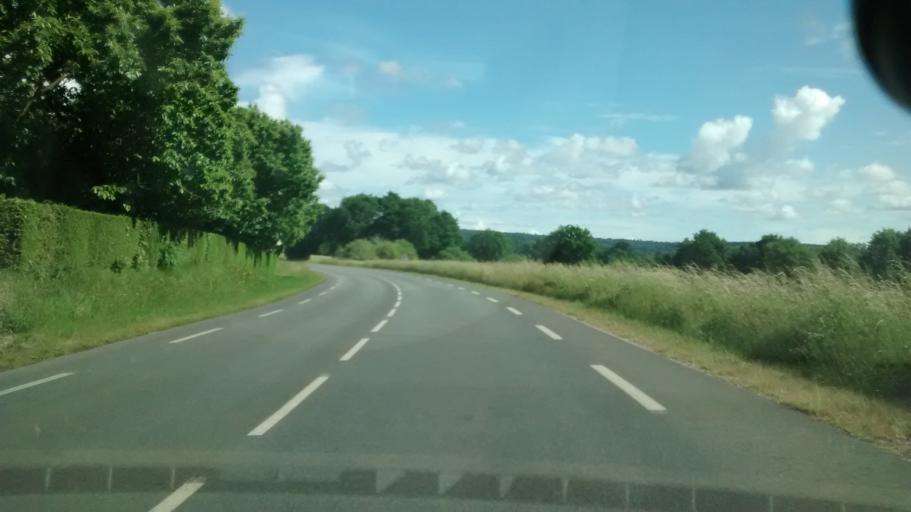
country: FR
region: Brittany
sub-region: Departement du Morbihan
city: Malestroit
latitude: 47.8341
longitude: -2.3925
